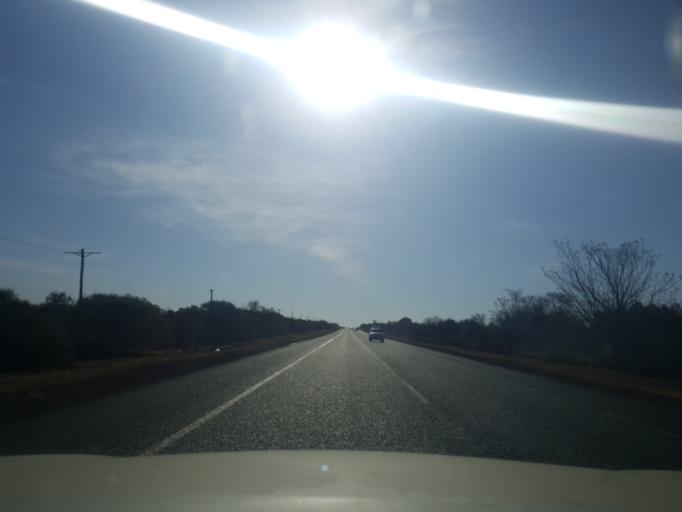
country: ZA
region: North-West
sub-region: Ngaka Modiri Molema District Municipality
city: Zeerust
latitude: -25.5268
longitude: 26.0146
